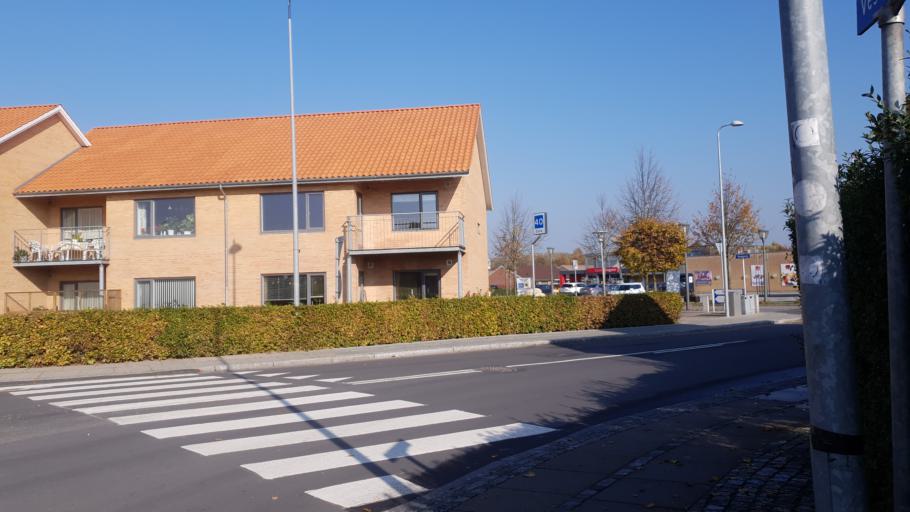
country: DK
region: Central Jutland
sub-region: Hedensted Kommune
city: Hedensted
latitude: 55.8037
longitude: 9.6923
